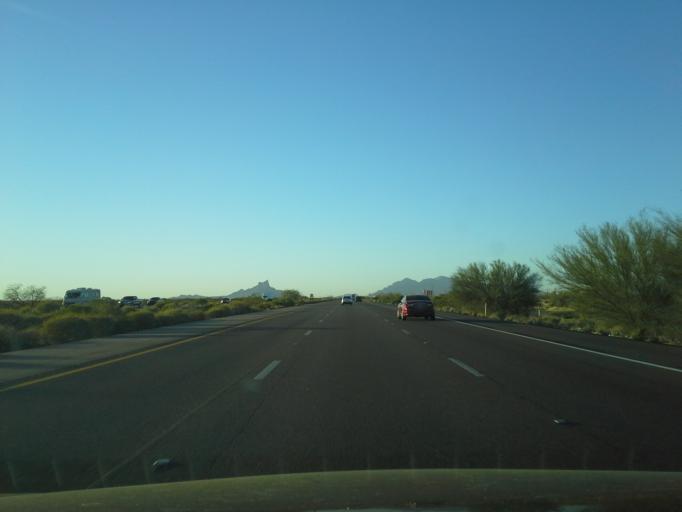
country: US
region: Arizona
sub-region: Pima County
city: Avra Valley
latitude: 32.5233
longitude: -111.2809
